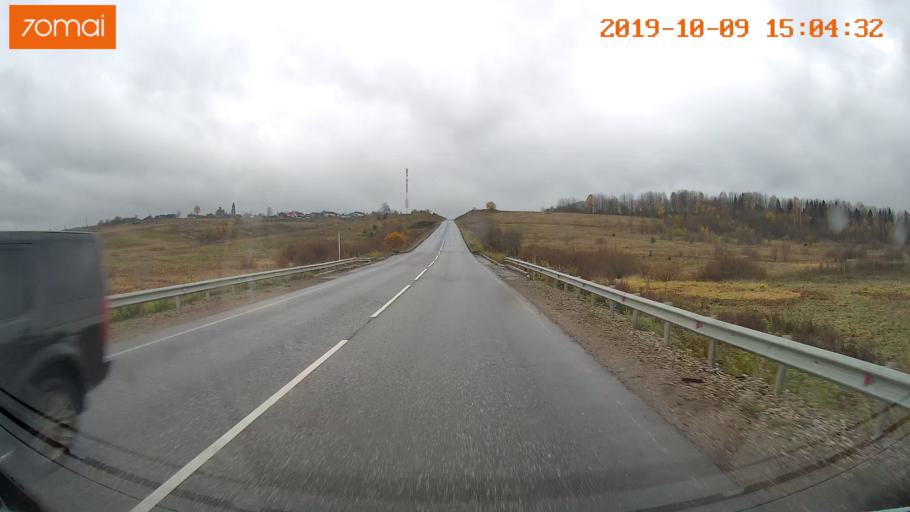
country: RU
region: Kostroma
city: Chistyye Bory
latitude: 58.2572
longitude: 41.6662
